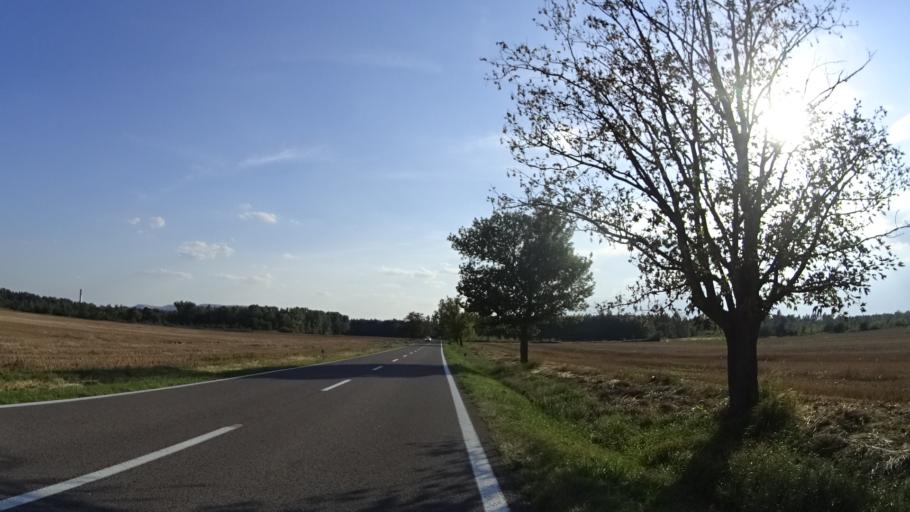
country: HU
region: Komarom-Esztergom
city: Nyergesujfalu
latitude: 47.7817
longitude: 18.5753
